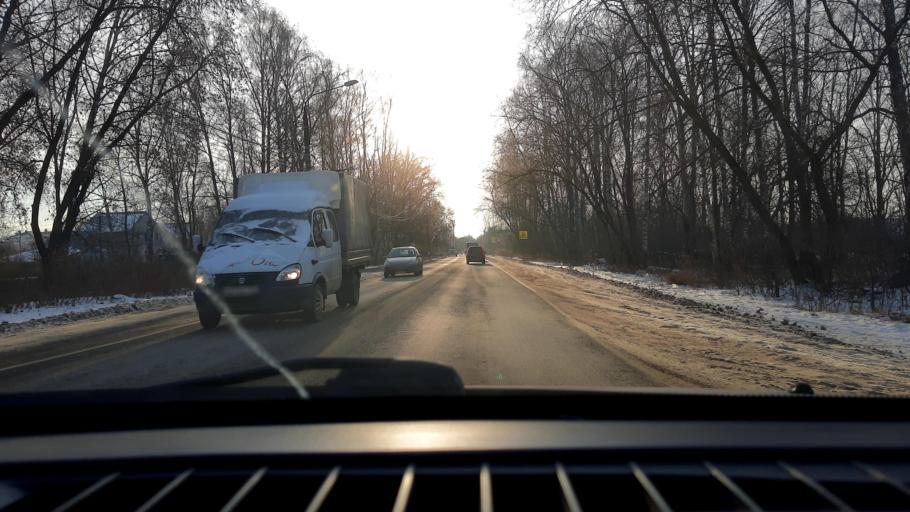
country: RU
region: Nizjnij Novgorod
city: Bor
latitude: 56.3640
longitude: 44.0871
